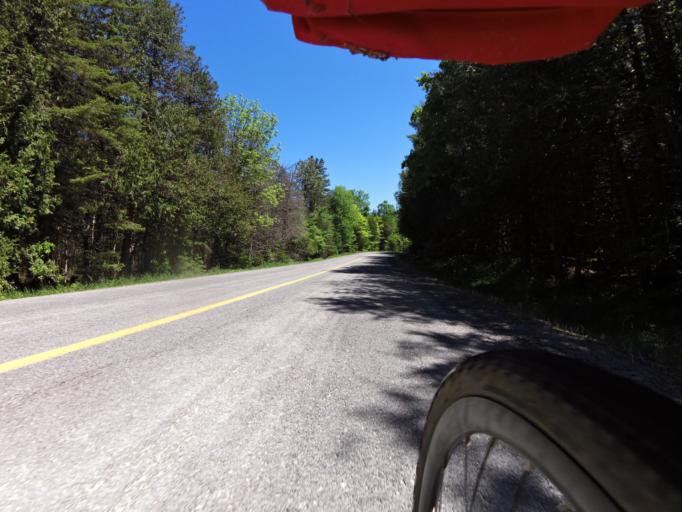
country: CA
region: Ontario
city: Arnprior
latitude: 45.1624
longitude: -76.4429
